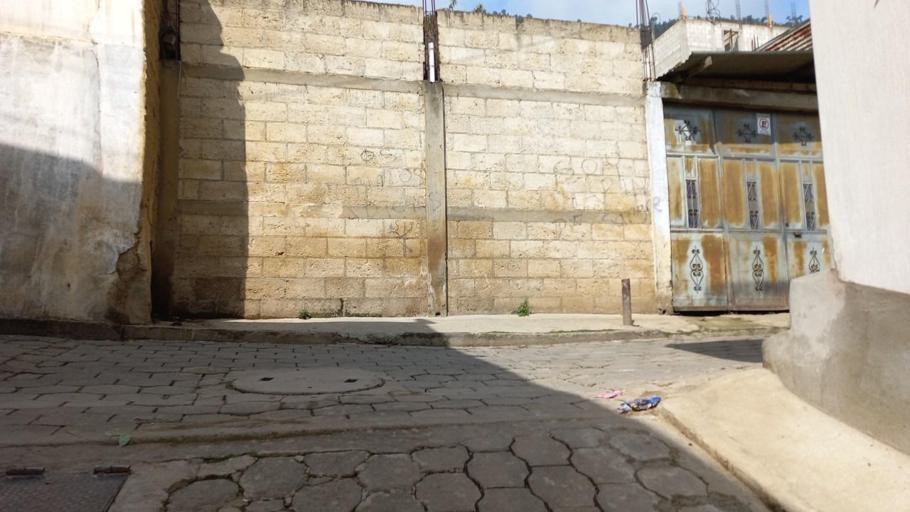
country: GT
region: Totonicapan
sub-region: Municipio de San Andres Xecul
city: San Andres Xecul
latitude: 14.9032
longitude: -91.4840
